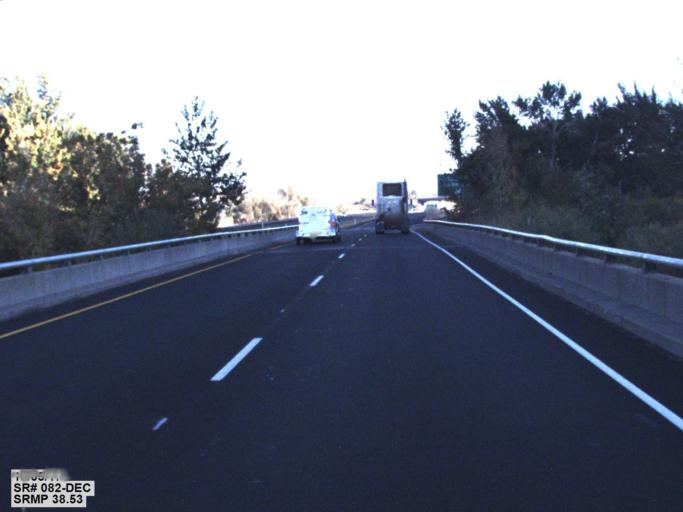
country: US
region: Washington
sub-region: Yakima County
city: Union Gap
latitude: 46.5309
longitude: -120.4713
